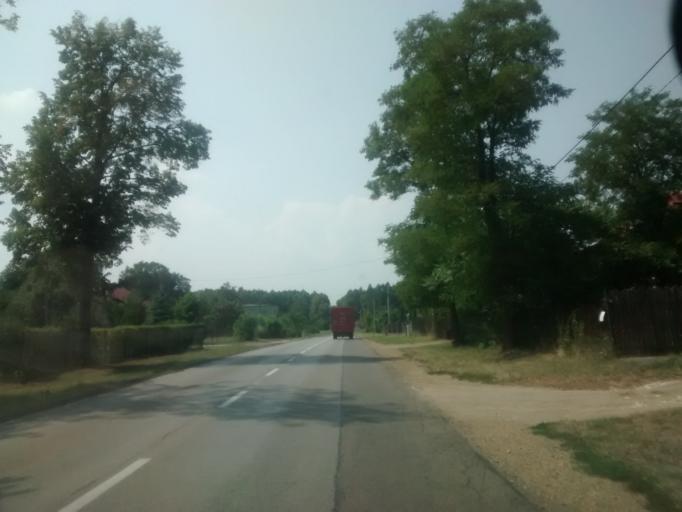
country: PL
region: Silesian Voivodeship
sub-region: Powiat czestochowski
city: Olsztyn
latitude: 50.7527
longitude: 19.2922
